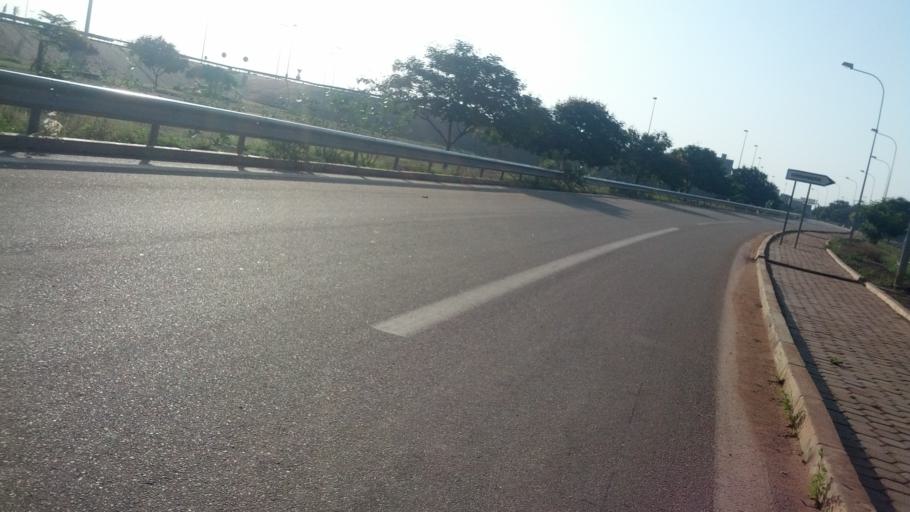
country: BF
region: Centre
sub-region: Kadiogo Province
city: Ouagadougou
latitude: 12.3324
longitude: -1.5053
